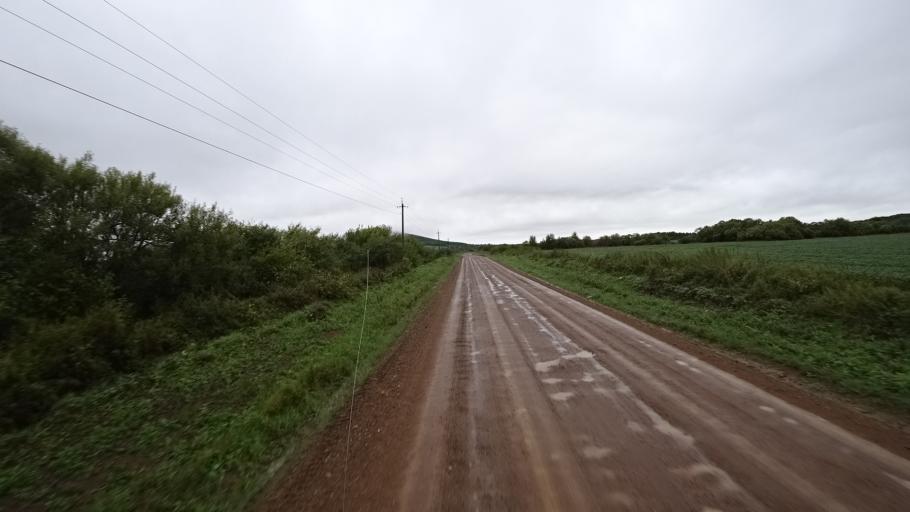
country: RU
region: Primorskiy
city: Monastyrishche
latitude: 44.2480
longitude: 132.4365
